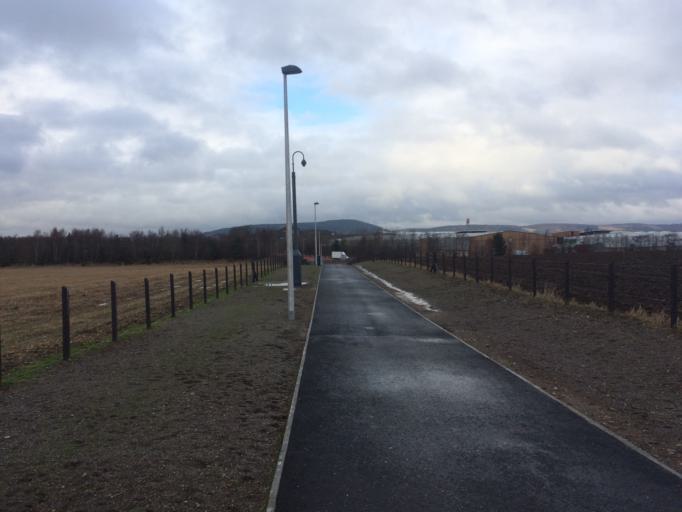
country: GB
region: Scotland
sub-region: Highland
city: Inverness
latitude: 57.4782
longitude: -4.1764
